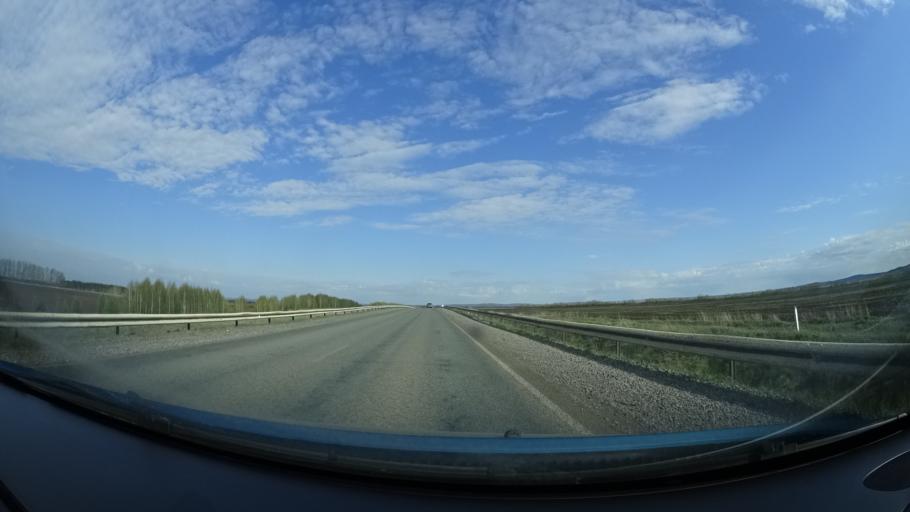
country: RU
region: Bashkortostan
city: Blagoveshchensk
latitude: 55.1942
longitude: 55.8357
